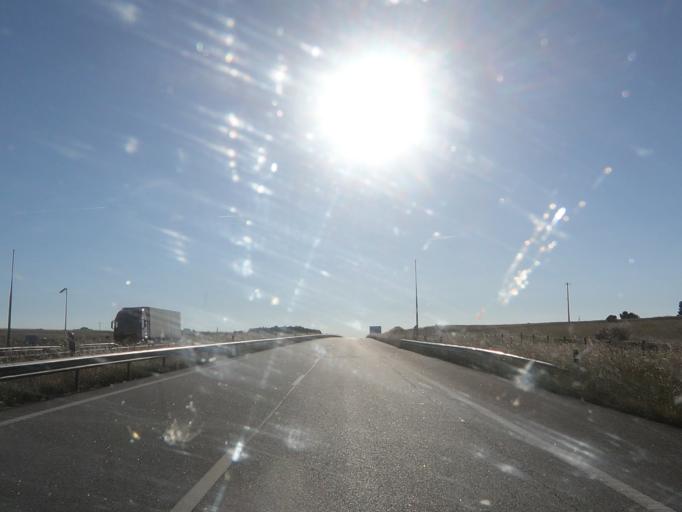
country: ES
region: Castille and Leon
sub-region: Provincia de Salamanca
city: Fuentes de Onoro
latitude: 40.6087
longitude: -6.9915
